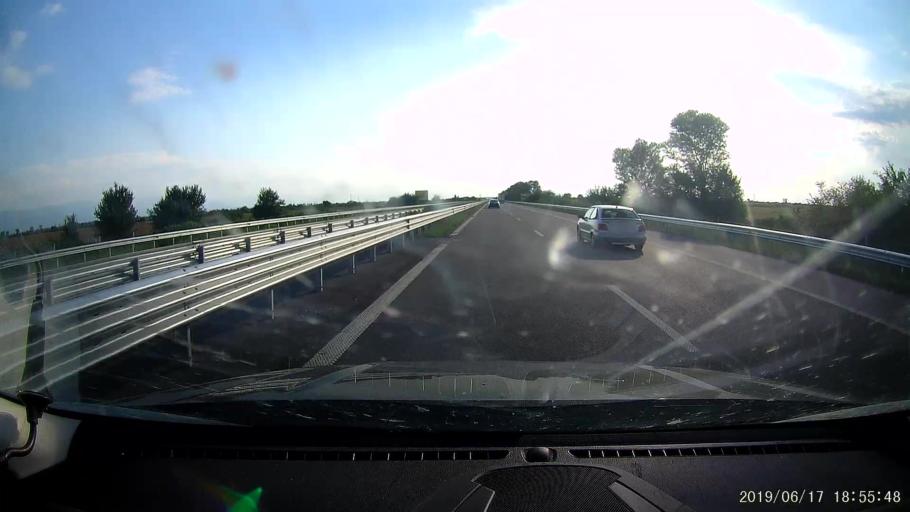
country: BG
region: Plovdiv
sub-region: Obshtina Plovdiv
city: Plovdiv
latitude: 42.2154
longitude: 24.8436
